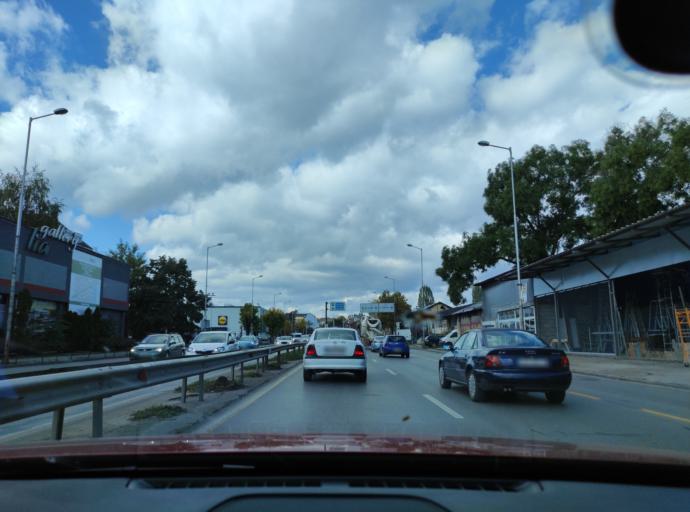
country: BG
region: Sofia-Capital
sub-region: Stolichna Obshtina
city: Sofia
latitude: 42.7037
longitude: 23.3358
